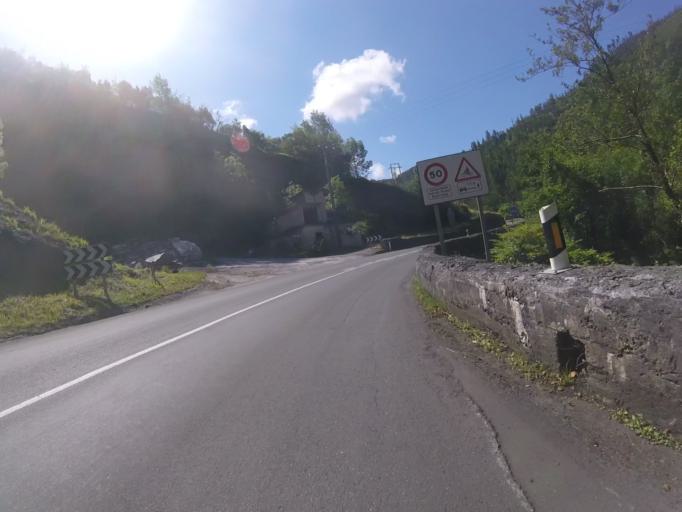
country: ES
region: Basque Country
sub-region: Provincia de Guipuzcoa
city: Azpeitia
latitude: 43.1777
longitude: -2.2237
